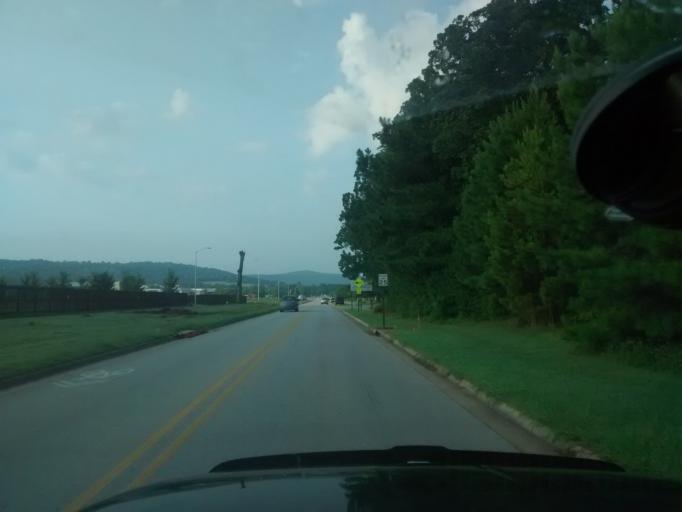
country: US
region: Arkansas
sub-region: Washington County
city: Farmington
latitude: 36.0775
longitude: -94.2175
